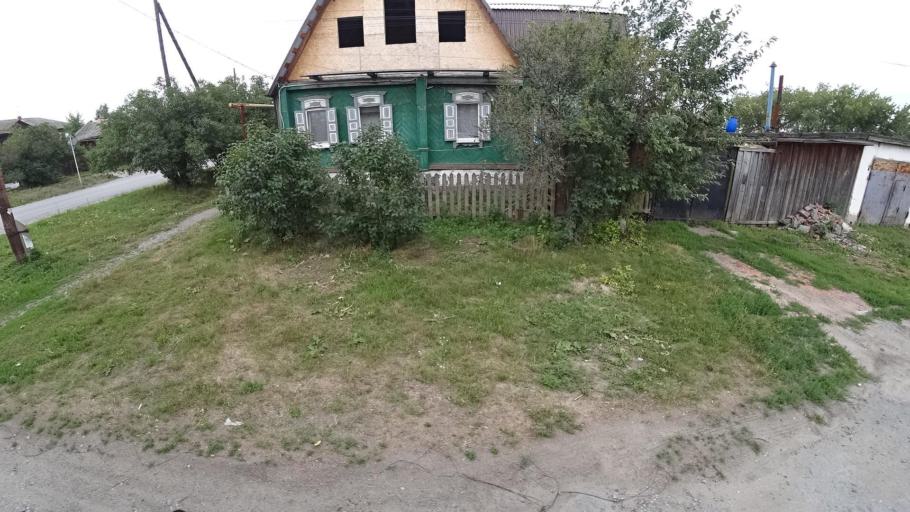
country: RU
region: Sverdlovsk
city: Kamyshlov
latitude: 56.8364
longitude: 62.7163
